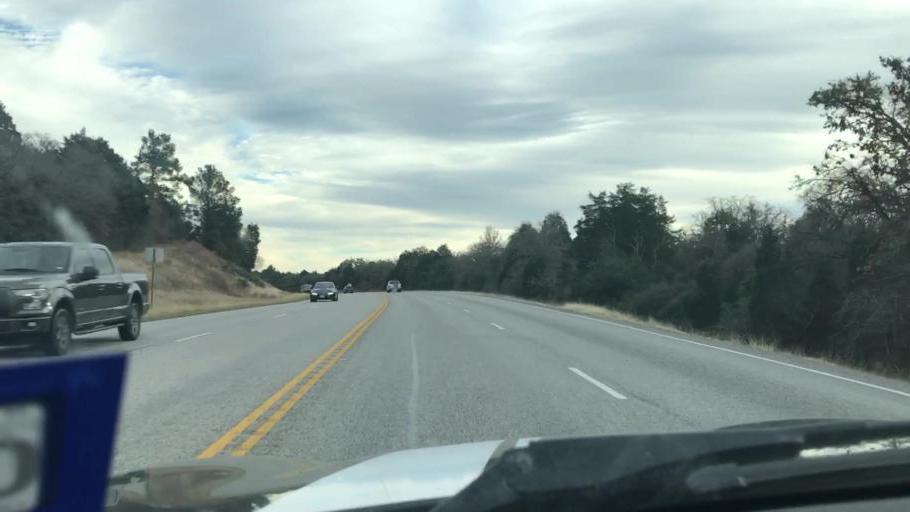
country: US
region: Texas
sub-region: Bastrop County
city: Camp Swift
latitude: 30.2499
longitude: -97.2242
